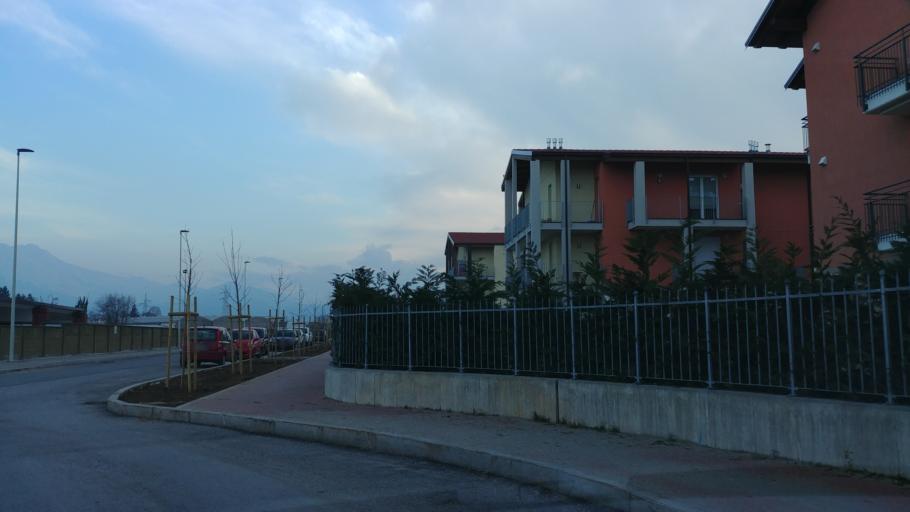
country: IT
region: Piedmont
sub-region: Provincia di Cuneo
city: Cuneo
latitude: 44.4014
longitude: 7.5354
